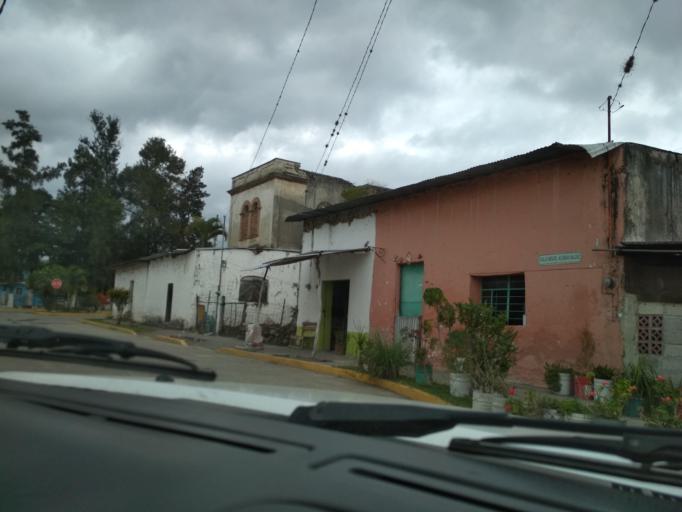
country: MX
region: Veracruz
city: El Castillo
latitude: 19.5822
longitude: -96.8376
